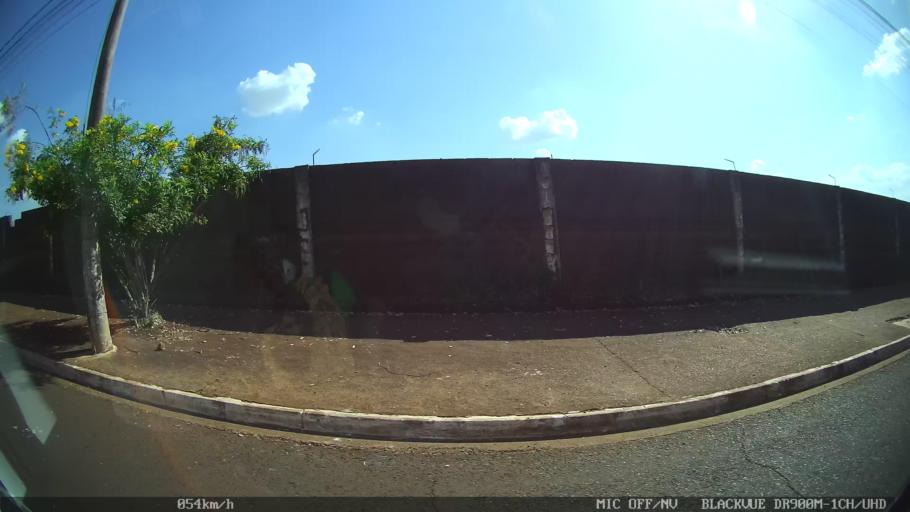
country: BR
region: Sao Paulo
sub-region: Ribeirao Preto
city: Ribeirao Preto
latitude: -21.1893
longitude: -47.8444
